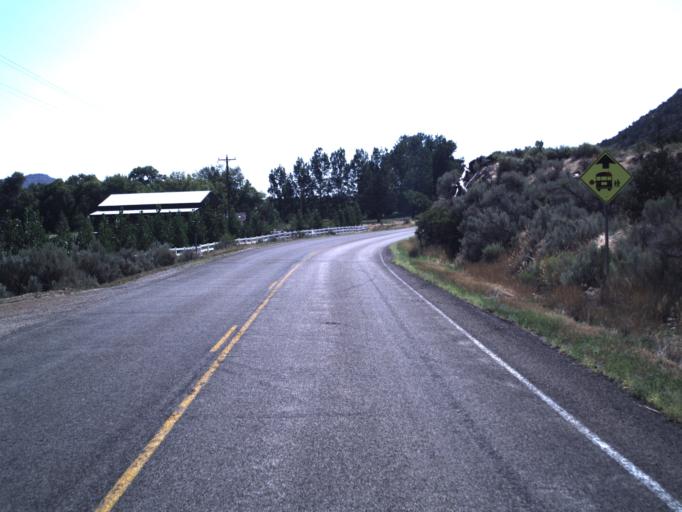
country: US
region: Utah
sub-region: Duchesne County
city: Duchesne
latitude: 40.2823
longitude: -110.4823
